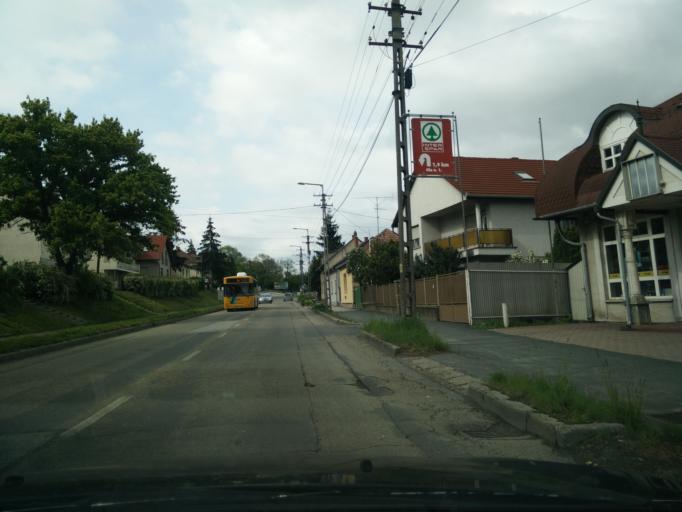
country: HU
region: Zala
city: Zalaegerszeg
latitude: 46.8521
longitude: 16.8452
